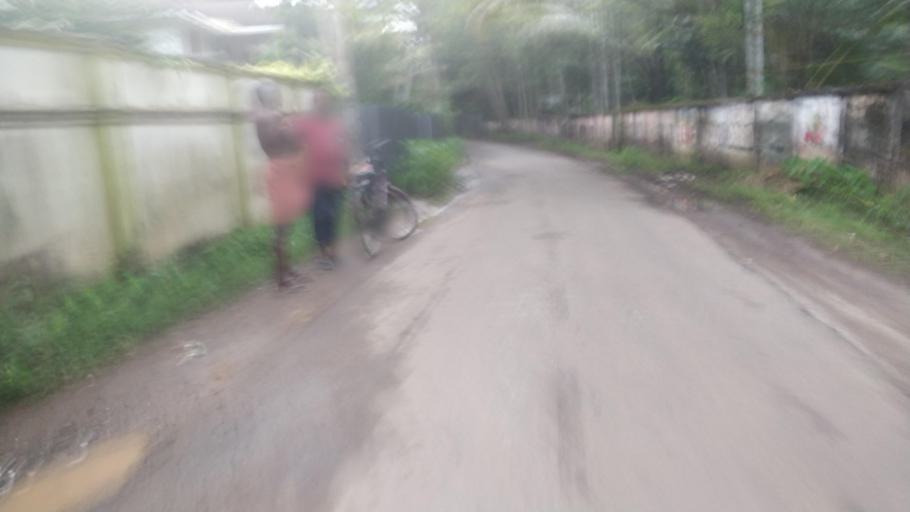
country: IN
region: Kerala
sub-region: Alappuzha
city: Shertallai
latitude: 9.6920
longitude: 76.3474
